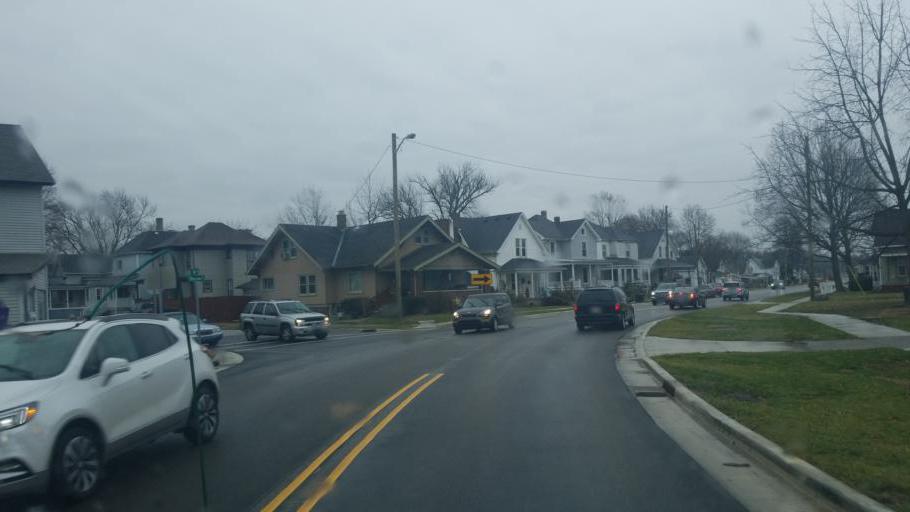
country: US
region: Indiana
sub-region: Shelby County
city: Shelbyville
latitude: 39.5159
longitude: -85.7754
